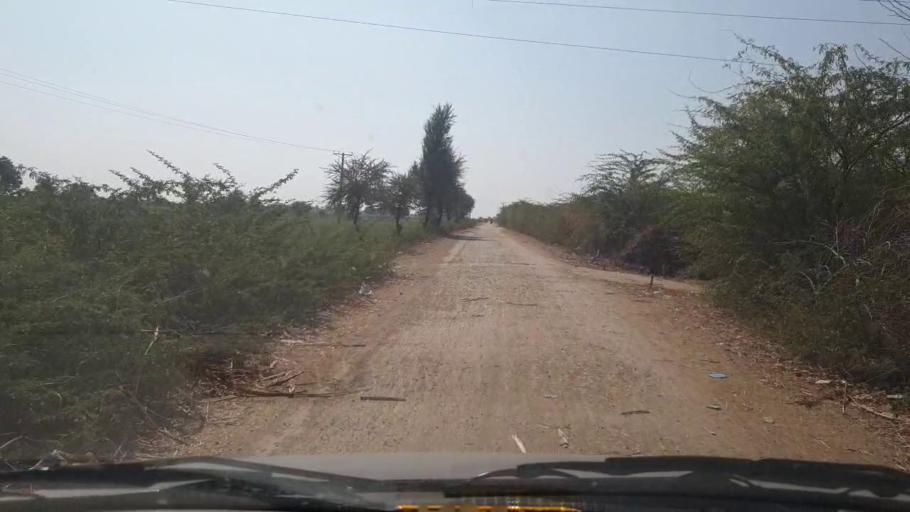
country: PK
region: Sindh
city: Samaro
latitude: 25.2301
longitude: 69.3362
